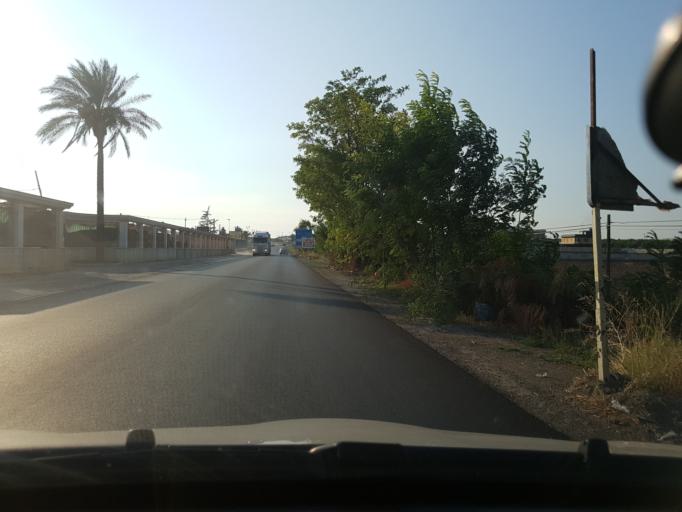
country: IT
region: Apulia
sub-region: Provincia di Foggia
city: Cerignola
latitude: 41.2706
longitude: 15.8801
